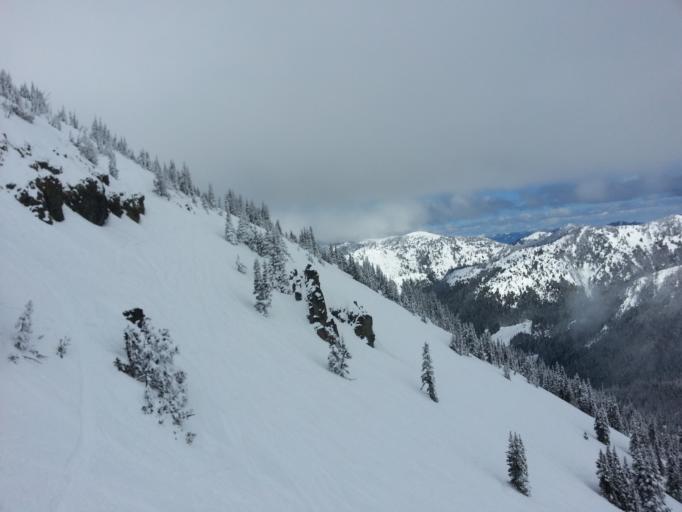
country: US
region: Washington
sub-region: King County
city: Enumclaw
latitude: 46.9264
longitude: -121.5038
